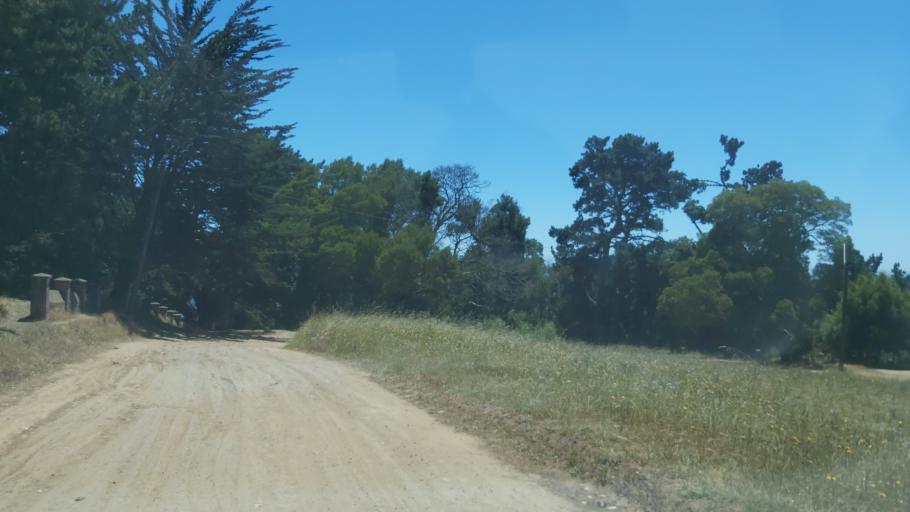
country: CL
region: Maule
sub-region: Provincia de Talca
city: Constitucion
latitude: -35.3219
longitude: -72.4130
